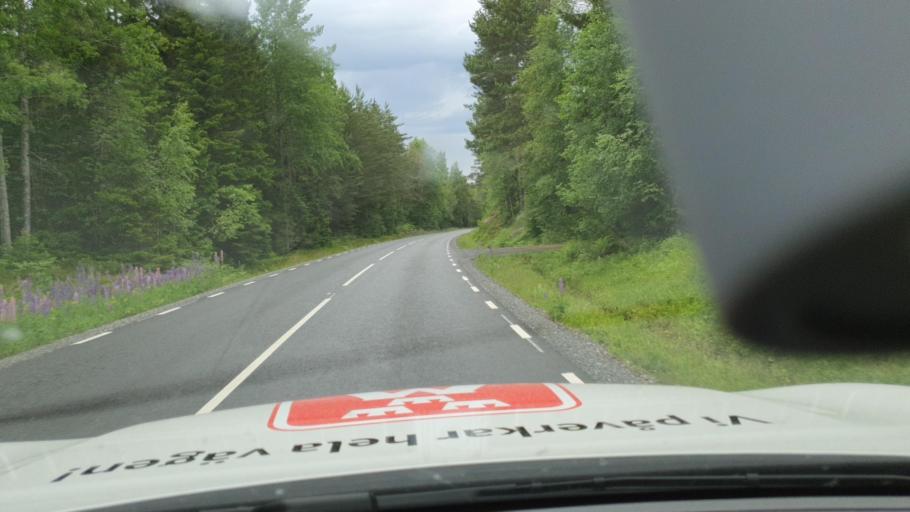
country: SE
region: OErebro
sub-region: Laxa Kommun
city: Laxa
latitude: 58.8830
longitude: 14.4976
